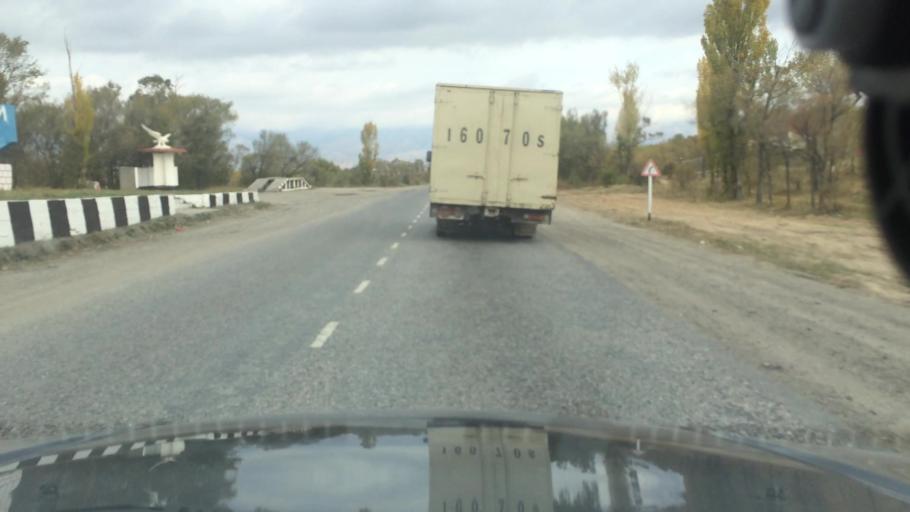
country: KG
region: Ysyk-Koel
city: Tyup
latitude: 42.6659
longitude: 78.3494
